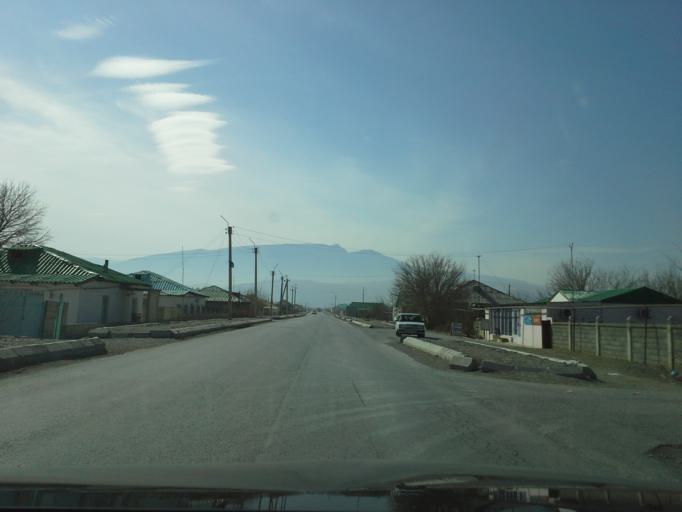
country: TM
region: Ahal
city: Abadan
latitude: 38.1122
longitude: 58.0344
